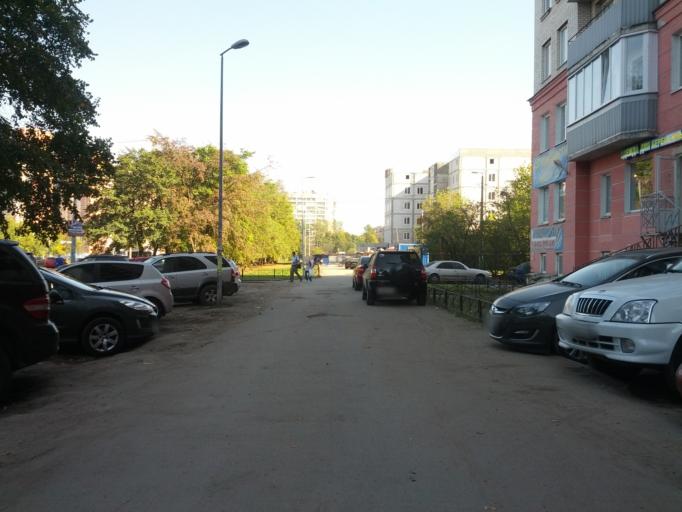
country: RU
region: St.-Petersburg
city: Kupchino
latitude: 59.8424
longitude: 30.3503
